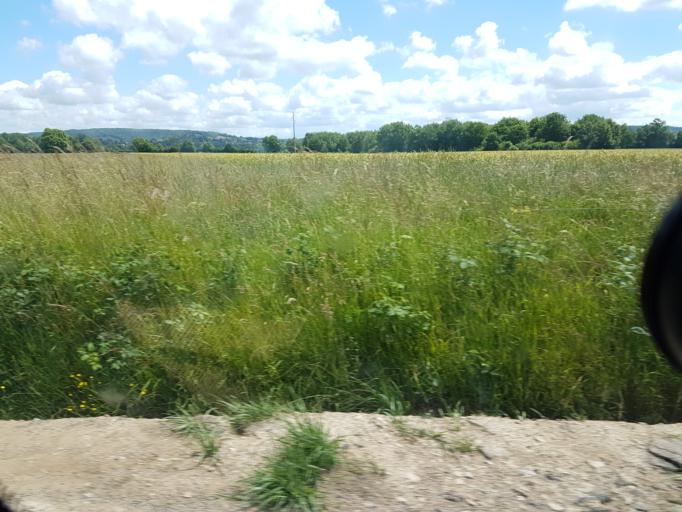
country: FR
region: Bourgogne
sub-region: Departement de Saone-et-Loire
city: Epinac
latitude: 46.9805
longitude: 4.4890
